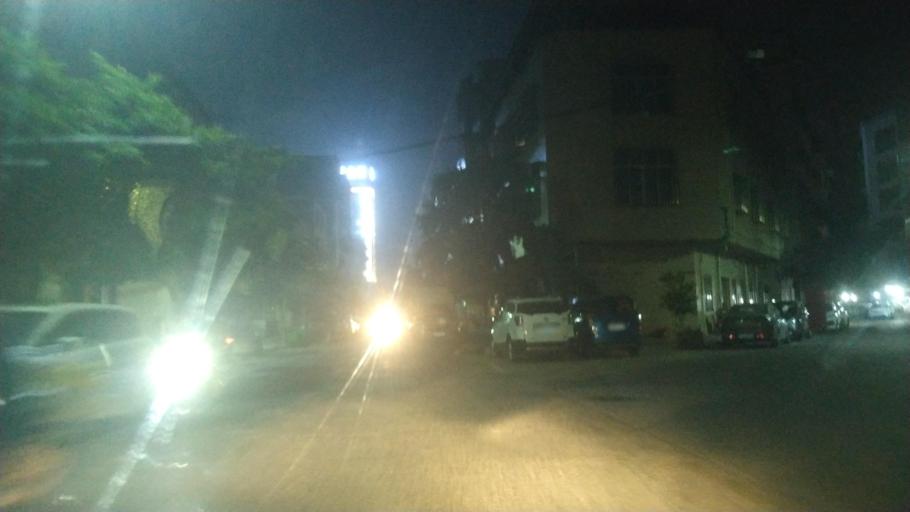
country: CN
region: Guangdong
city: Xiaguo
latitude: 21.6463
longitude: 110.6309
